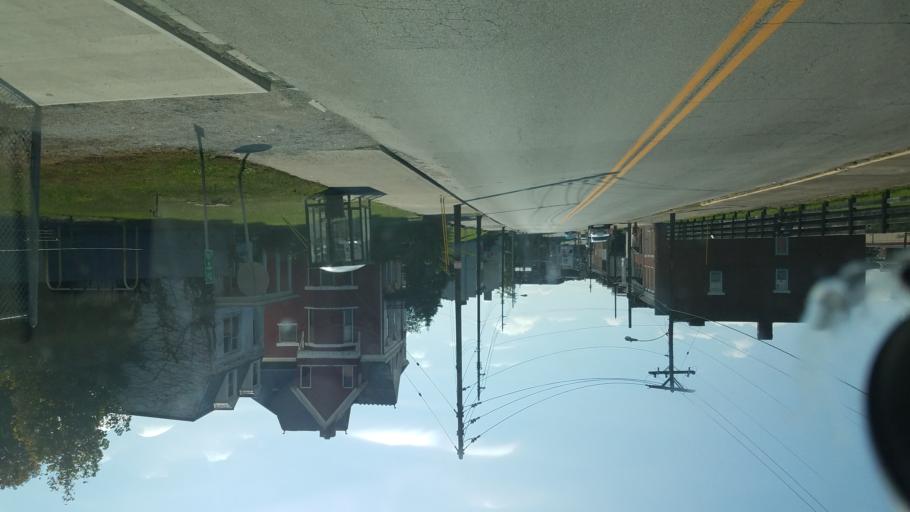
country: US
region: Ohio
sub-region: Brown County
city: Aberdeen
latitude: 38.6503
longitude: -83.7698
